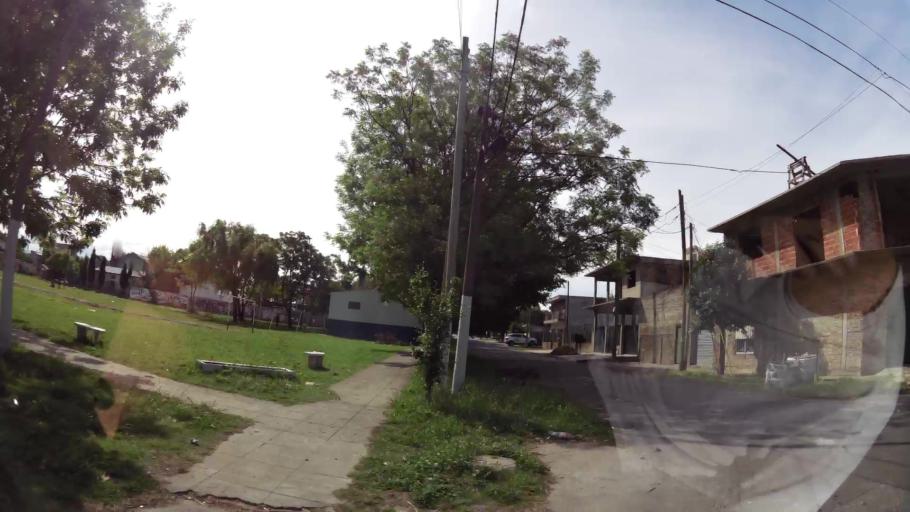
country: AR
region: Buenos Aires
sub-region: Partido de Quilmes
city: Quilmes
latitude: -34.7622
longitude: -58.2369
